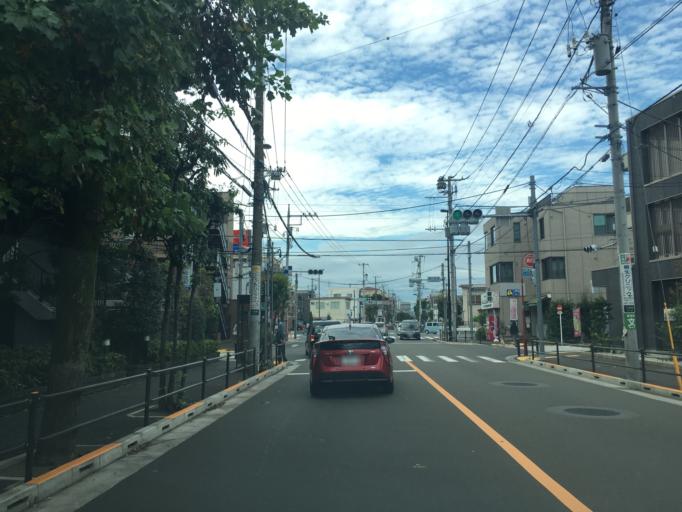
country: JP
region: Tokyo
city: Chofugaoka
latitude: 35.6508
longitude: 139.5373
